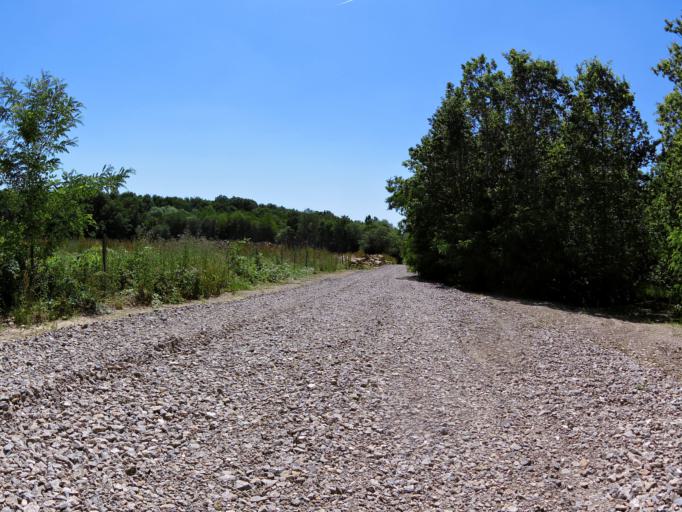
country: DE
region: Bavaria
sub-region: Regierungsbezirk Unterfranken
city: Kleinrinderfeld
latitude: 49.7023
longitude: 9.8608
